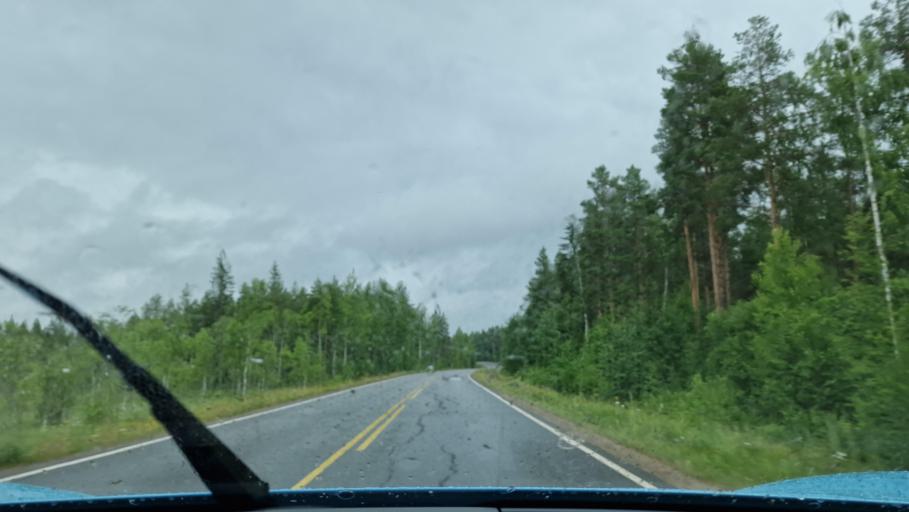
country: FI
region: Southern Ostrobothnia
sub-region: Jaerviseutu
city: Soini
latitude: 62.8070
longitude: 24.3617
